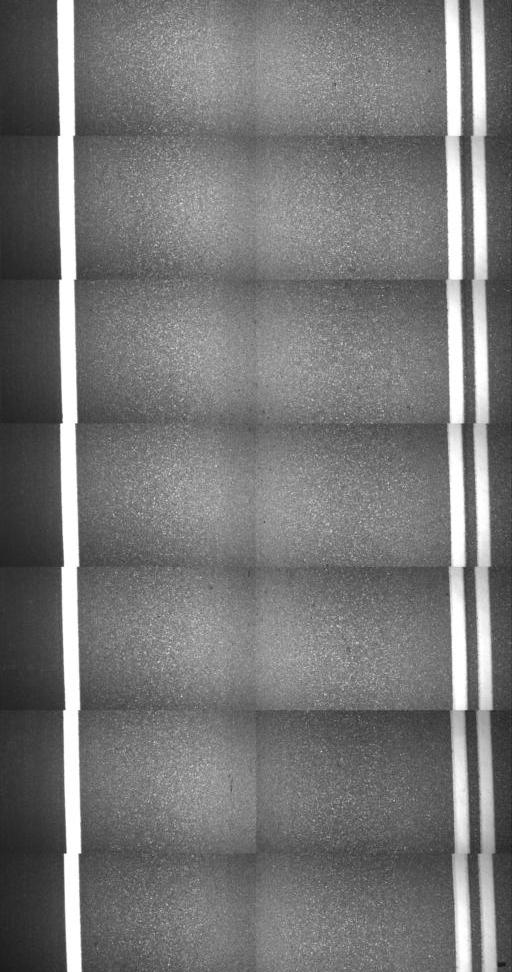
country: US
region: Vermont
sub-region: Windham County
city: Dover
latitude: 43.0793
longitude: -72.8650
